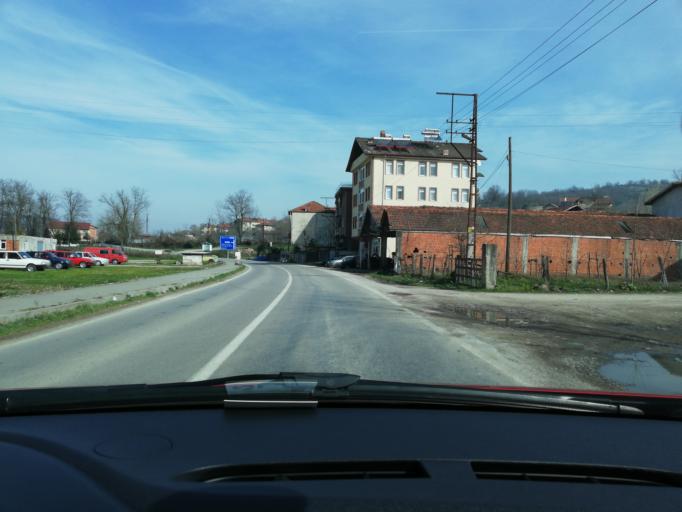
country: TR
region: Bartin
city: Kozcagiz
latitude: 41.4821
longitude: 32.3439
